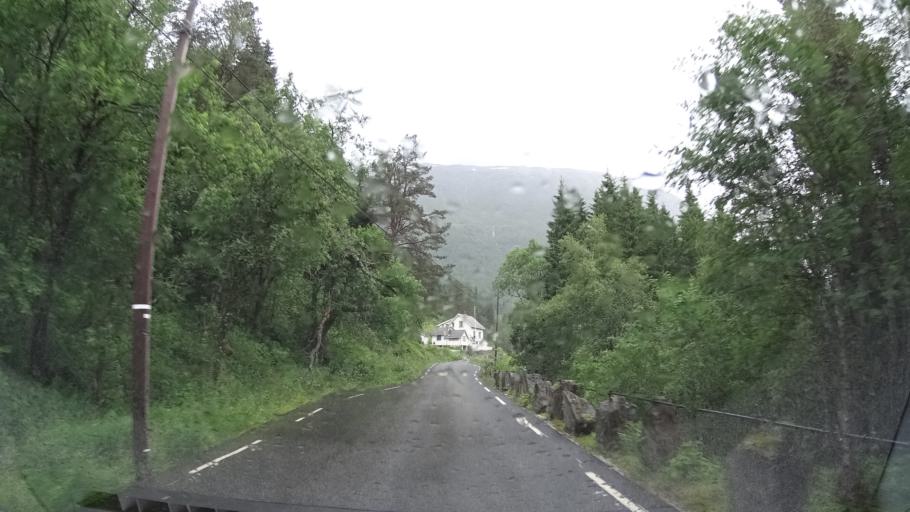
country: NO
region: Sogn og Fjordane
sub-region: Vik
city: Vik
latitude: 60.8284
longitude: 6.6835
